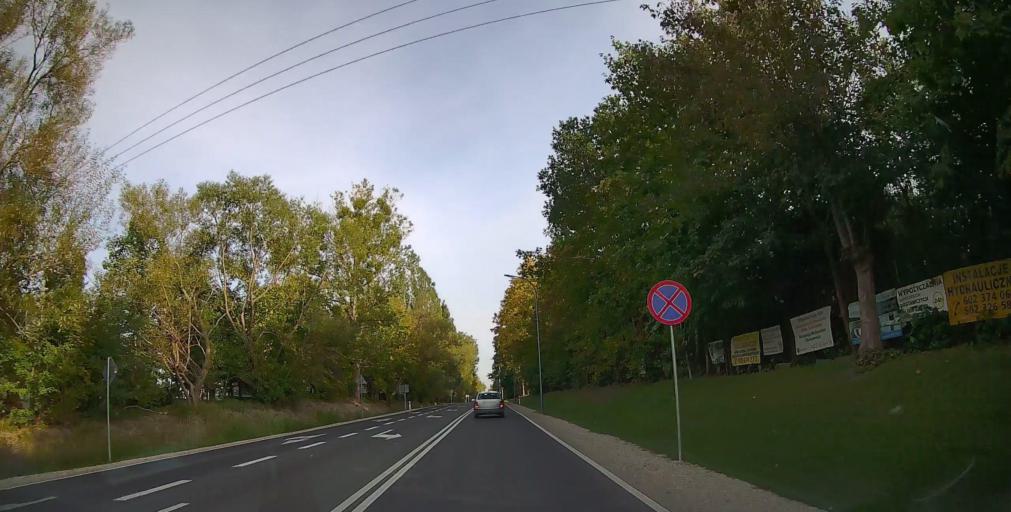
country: PL
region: Masovian Voivodeship
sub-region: Powiat piaseczynski
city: Zabieniec
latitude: 52.0583
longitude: 21.0483
